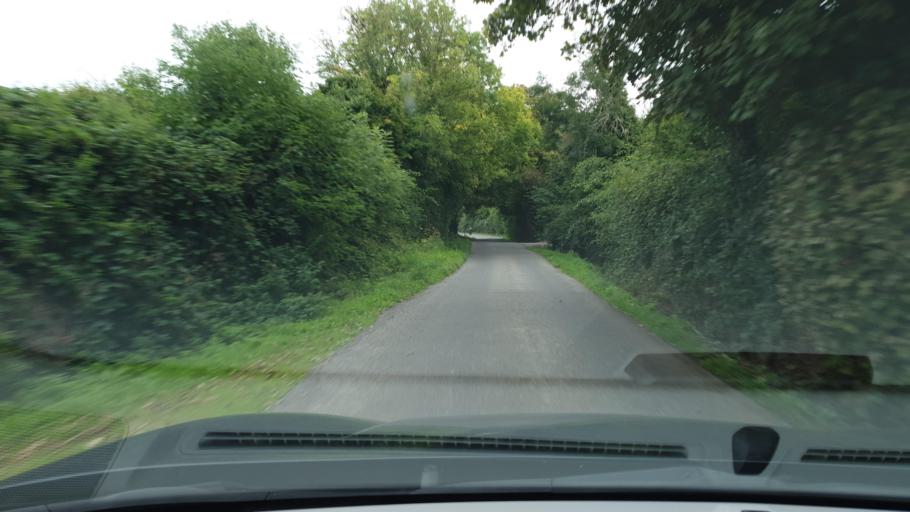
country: IE
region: Leinster
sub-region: An Mhi
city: Dunshaughlin
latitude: 53.4923
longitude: -6.5440
